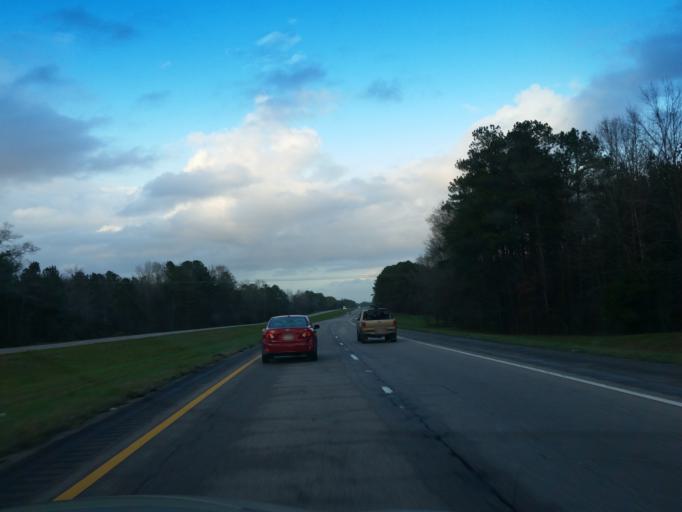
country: US
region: Mississippi
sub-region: Clarke County
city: Stonewall
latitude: 31.9910
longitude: -88.9455
